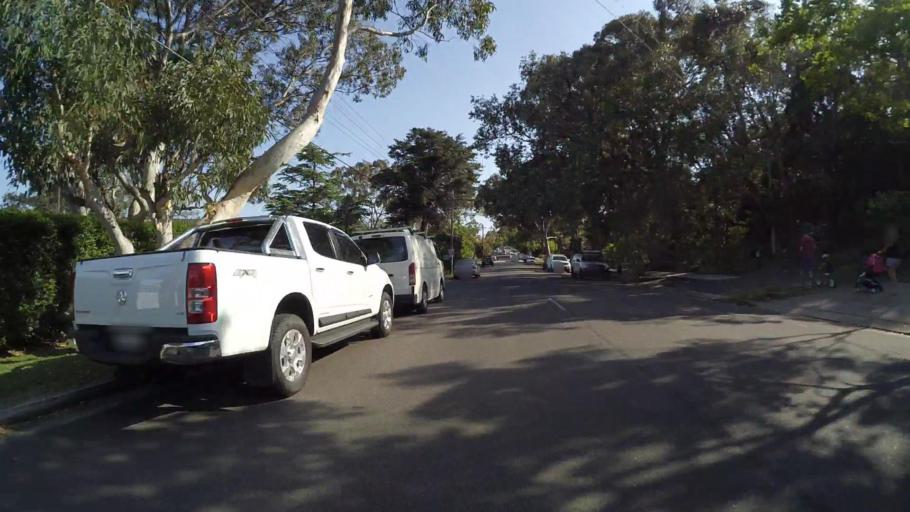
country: AU
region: New South Wales
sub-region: Sutherland Shire
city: Cronulla
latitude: -34.0567
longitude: 151.1396
